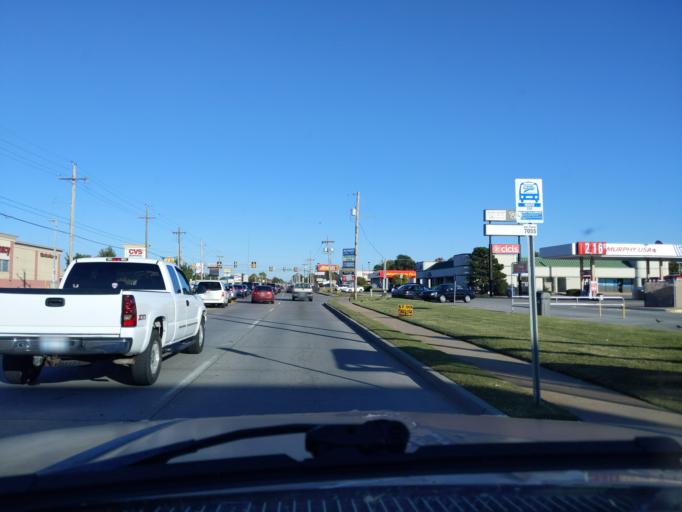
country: US
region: Oklahoma
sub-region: Tulsa County
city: Broken Arrow
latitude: 36.1189
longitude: -95.8528
